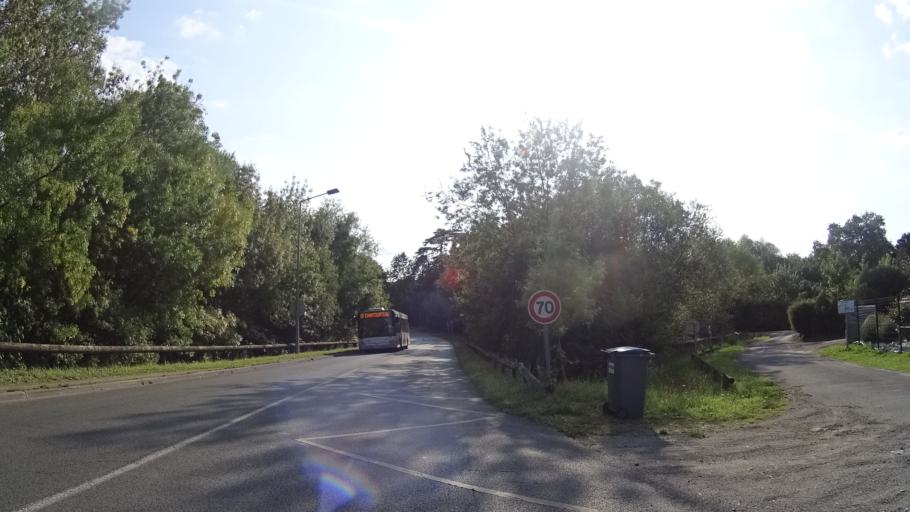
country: FR
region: Pays de la Loire
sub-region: Departement de Maine-et-Loire
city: Bouchemaine
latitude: 47.4131
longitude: -0.6173
